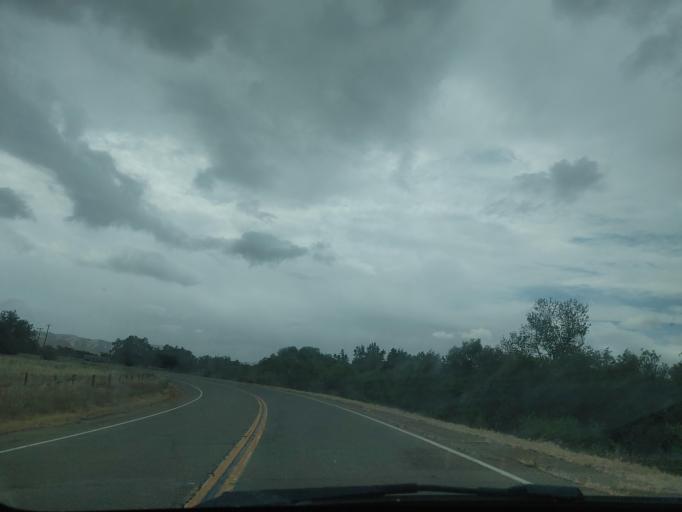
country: US
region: California
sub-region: Stanislaus County
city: Newman
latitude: 37.3298
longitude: -121.1057
